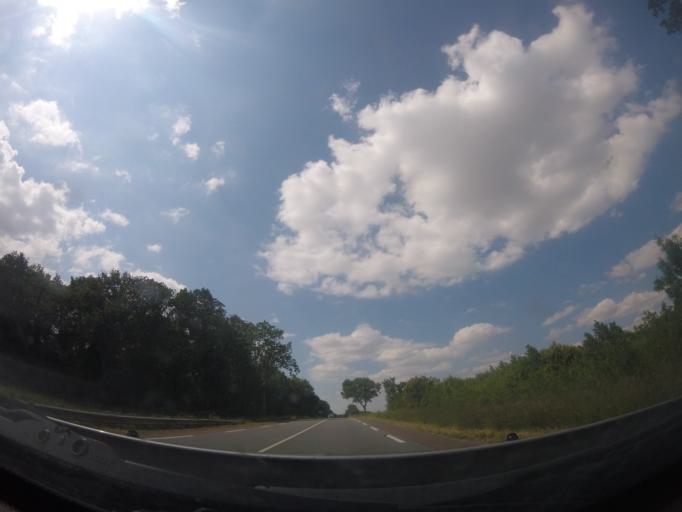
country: FR
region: Poitou-Charentes
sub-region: Departement de la Charente-Maritime
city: Saint-Porchaire
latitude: 45.8416
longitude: -0.8120
